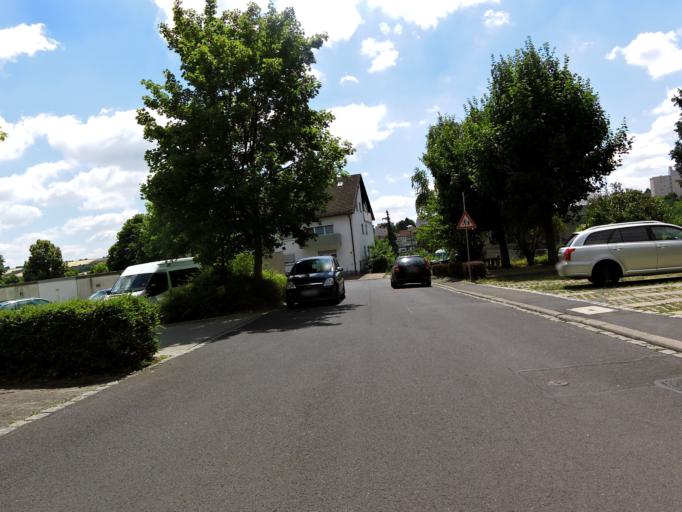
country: DE
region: Bavaria
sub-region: Regierungsbezirk Unterfranken
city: Gerbrunn
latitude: 49.7799
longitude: 9.9895
